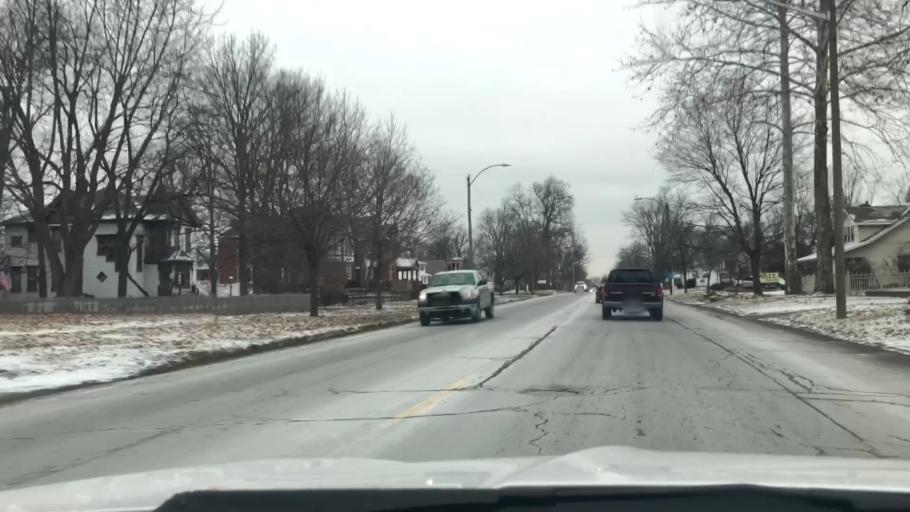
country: US
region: Indiana
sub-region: Fulton County
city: Rochester
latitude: 41.0587
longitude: -86.2167
